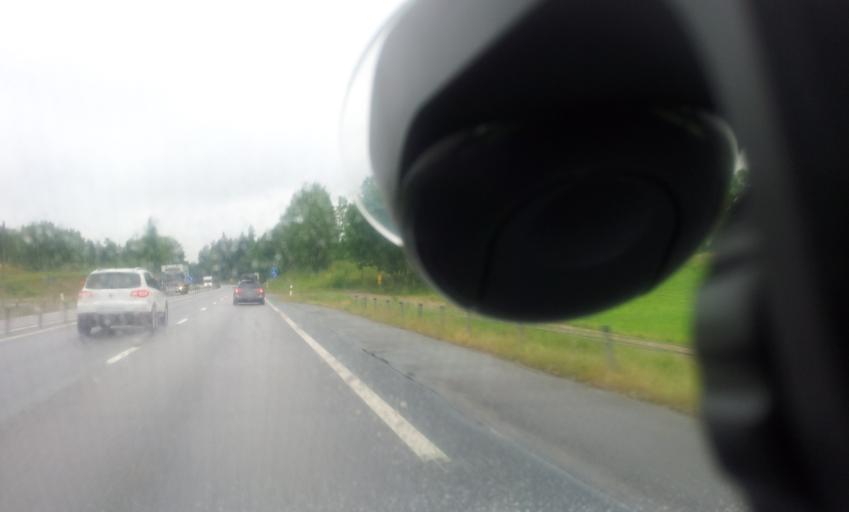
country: SE
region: Kalmar
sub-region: Vasterviks Kommun
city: Forserum
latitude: 57.9880
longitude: 16.4839
